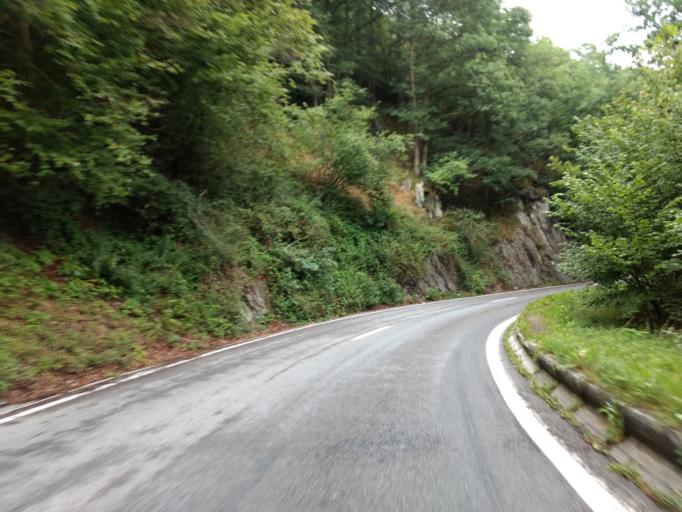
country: BE
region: Wallonia
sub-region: Province du Luxembourg
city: Houffalize
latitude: 50.1382
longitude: 5.7223
